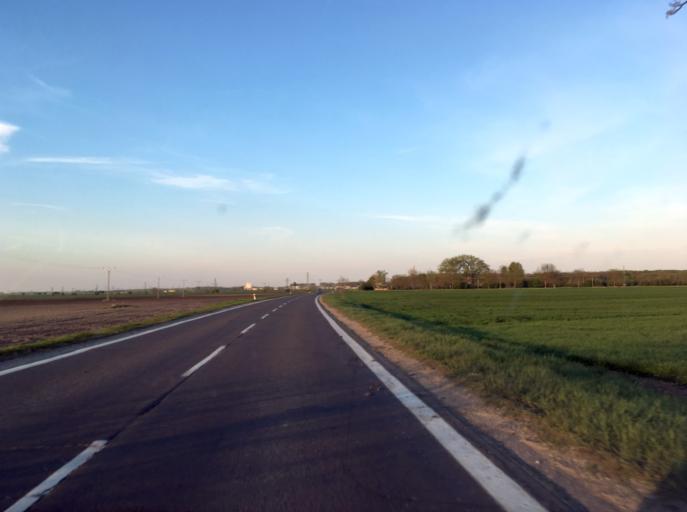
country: SK
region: Trnavsky
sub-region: Okres Dunajska Streda
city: Velky Meder
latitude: 47.8538
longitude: 17.7405
